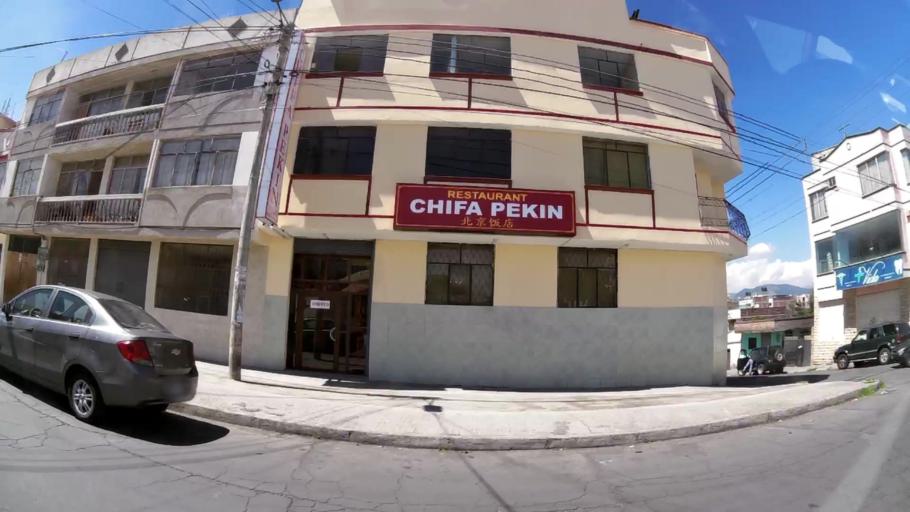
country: EC
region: Chimborazo
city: Riobamba
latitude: -1.6639
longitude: -78.6465
